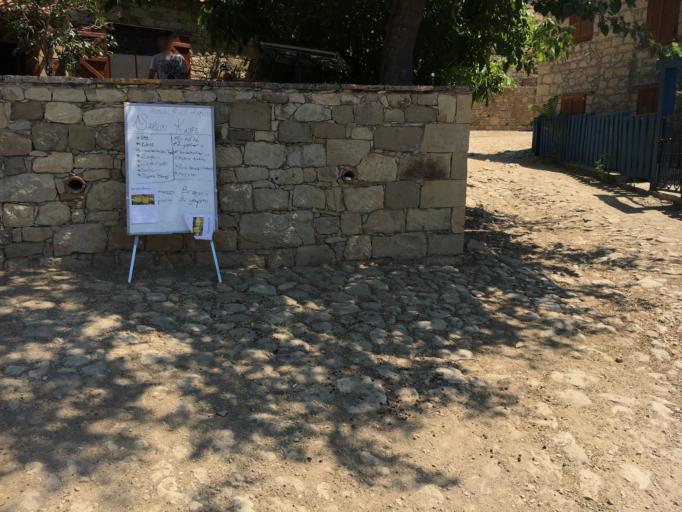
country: TR
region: Canakkale
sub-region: Merkez
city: Kucukkuyu
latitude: 39.5694
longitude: 26.6194
